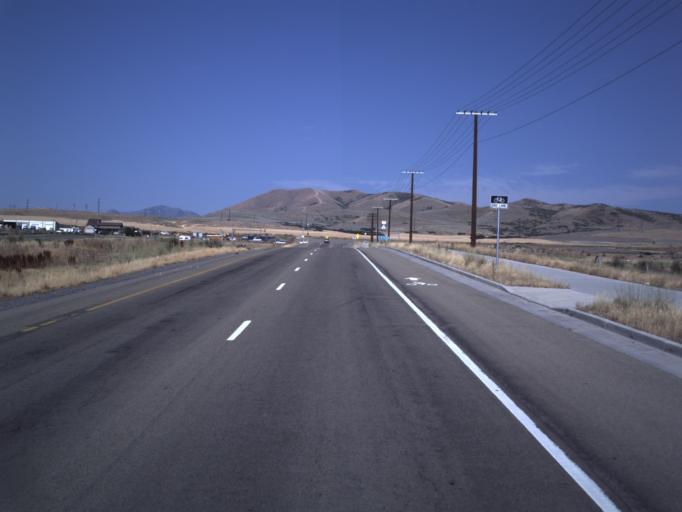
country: US
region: Utah
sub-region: Utah County
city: Saratoga Springs
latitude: 40.4135
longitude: -111.9180
